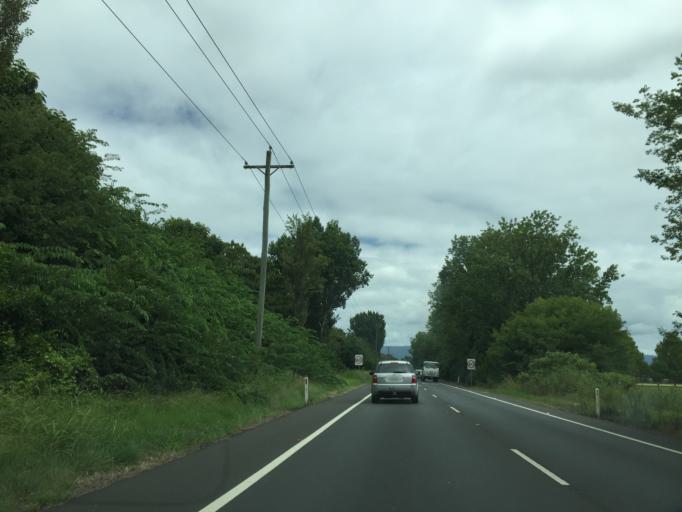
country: AU
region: New South Wales
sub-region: Hawkesbury
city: Richmond
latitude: -33.5903
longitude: 150.7331
